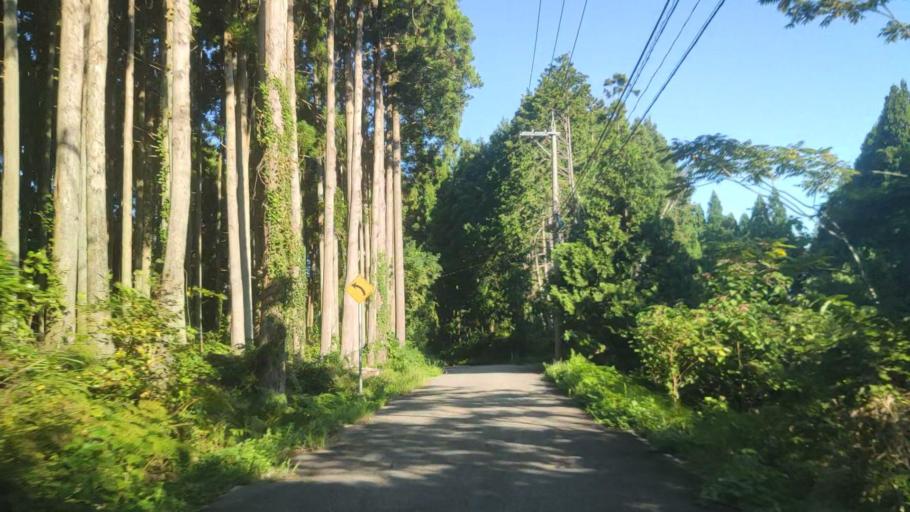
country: JP
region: Ishikawa
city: Nanao
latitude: 37.1340
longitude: 136.9104
